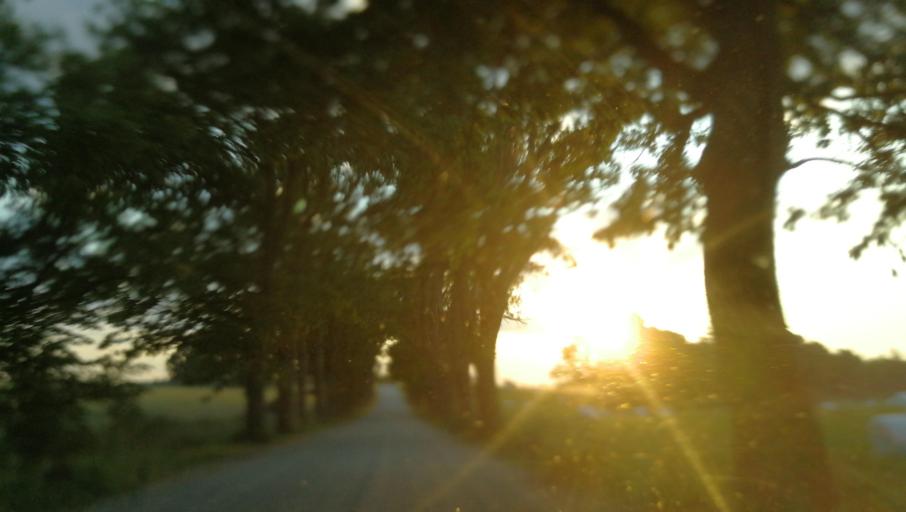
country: LV
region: Amatas Novads
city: Drabesi
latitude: 57.2498
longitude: 25.1848
